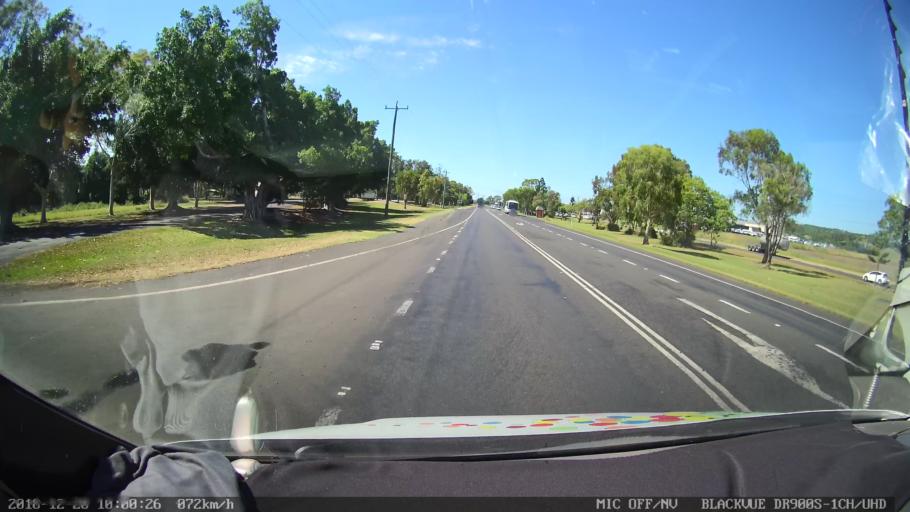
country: AU
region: New South Wales
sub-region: Lismore Municipality
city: Lismore
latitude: -28.8325
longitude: 153.2648
